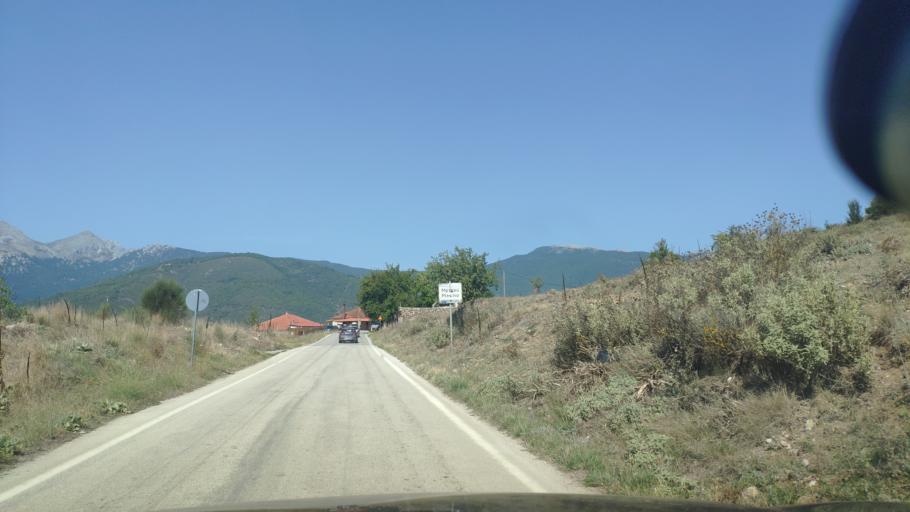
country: GR
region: West Greece
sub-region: Nomos Achaias
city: Aiyira
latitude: 37.9021
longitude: 22.3329
